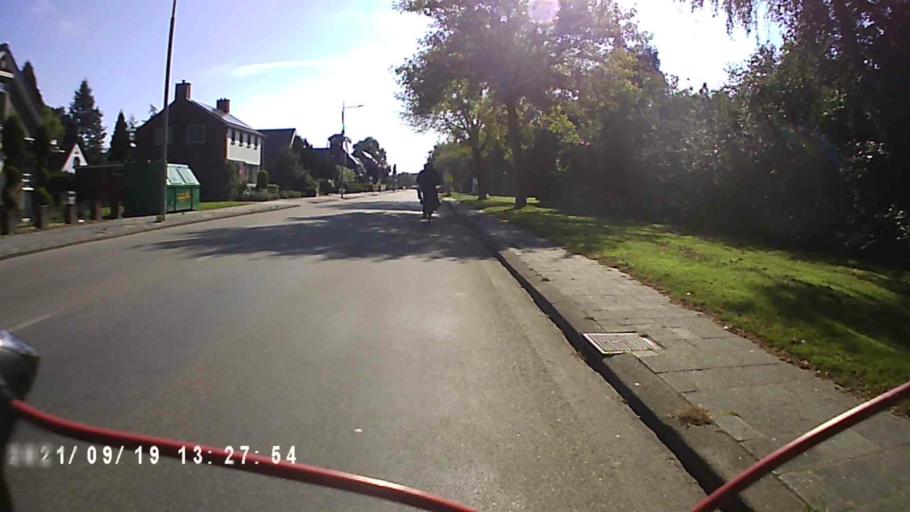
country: NL
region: Groningen
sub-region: Gemeente  Oldambt
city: Winschoten
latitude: 53.1499
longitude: 7.0220
